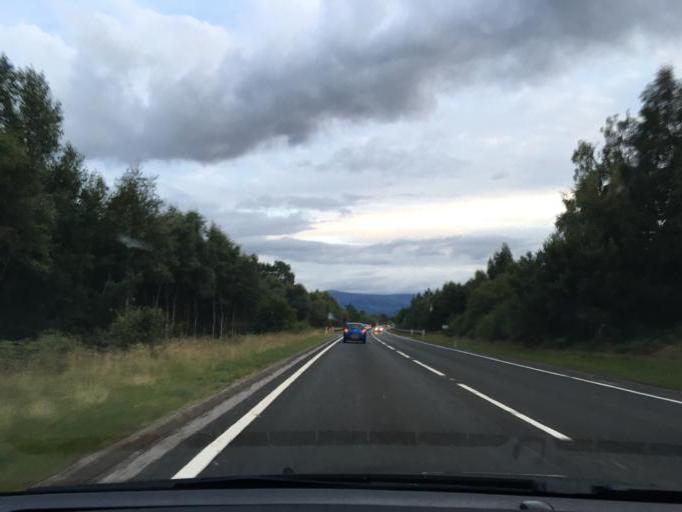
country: GB
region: Scotland
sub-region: Highland
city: Aviemore
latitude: 57.2469
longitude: -3.8068
